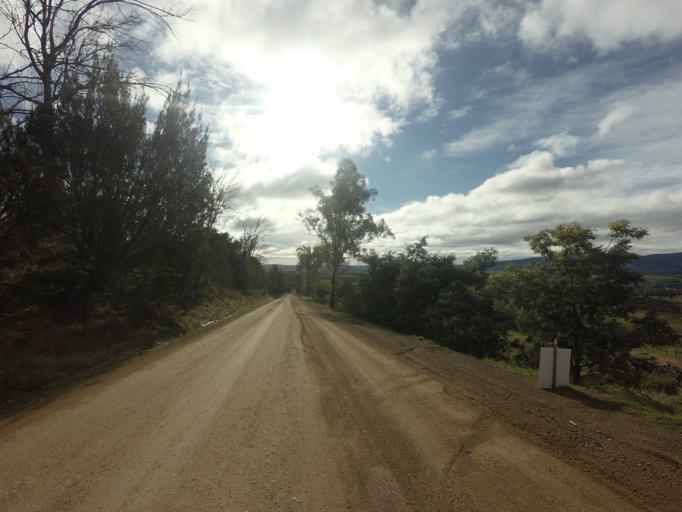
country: AU
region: Tasmania
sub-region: Derwent Valley
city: New Norfolk
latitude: -42.7216
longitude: 146.8734
